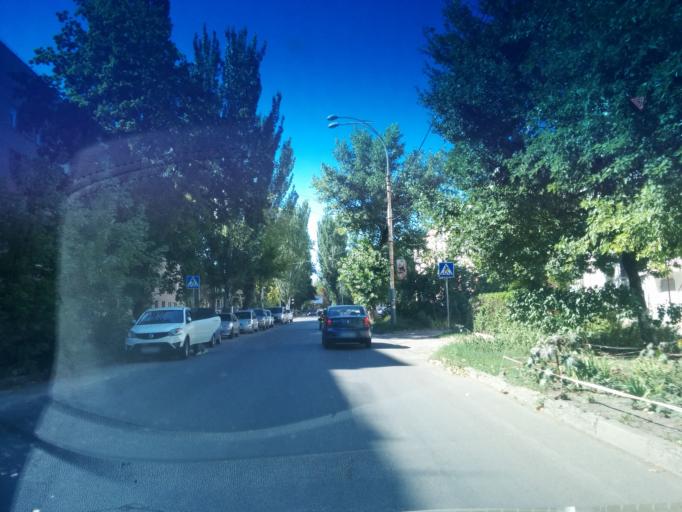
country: RU
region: Rostov
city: Shakhty
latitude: 47.7116
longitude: 40.2147
